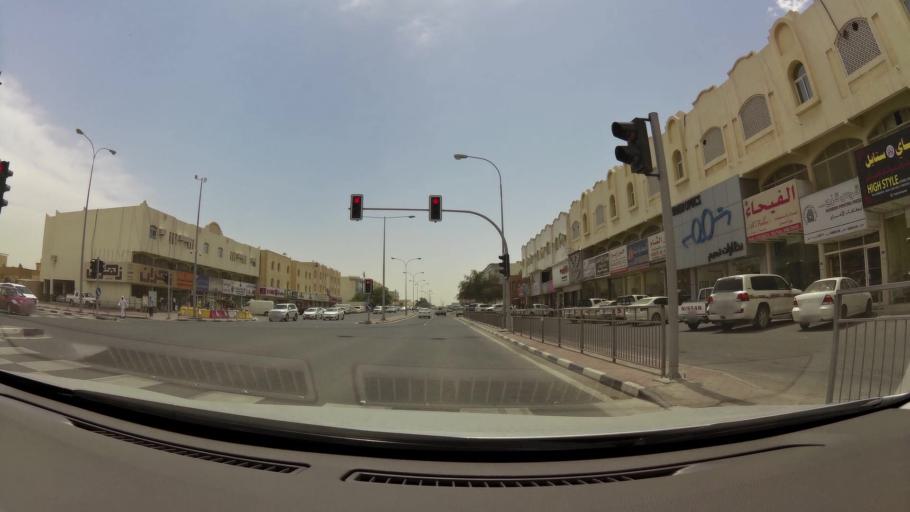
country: QA
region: Baladiyat ar Rayyan
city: Ar Rayyan
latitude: 25.2896
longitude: 51.4203
